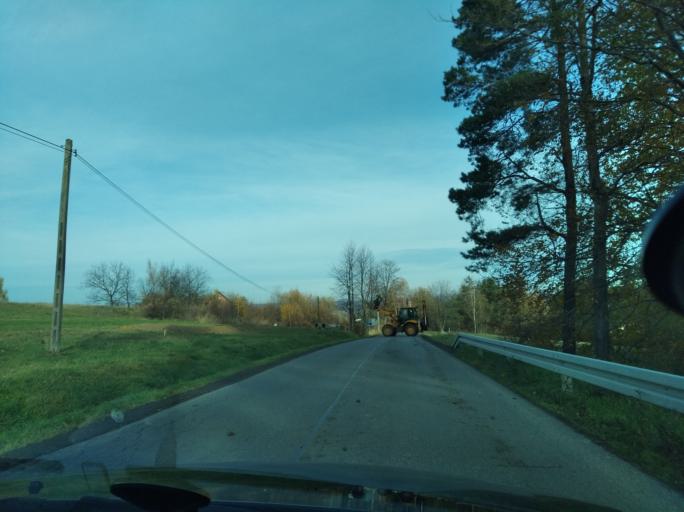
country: PL
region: Subcarpathian Voivodeship
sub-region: Powiat rzeszowski
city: Siedliska
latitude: 49.9412
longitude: 21.9782
